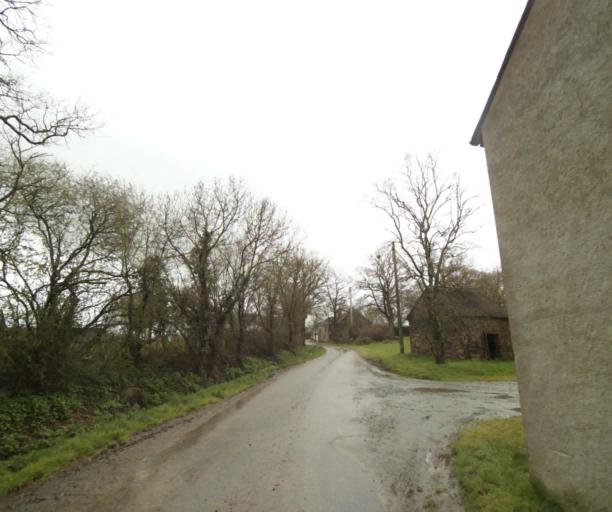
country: FR
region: Pays de la Loire
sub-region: Departement de la Loire-Atlantique
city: Bouvron
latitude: 47.4552
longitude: -1.8928
